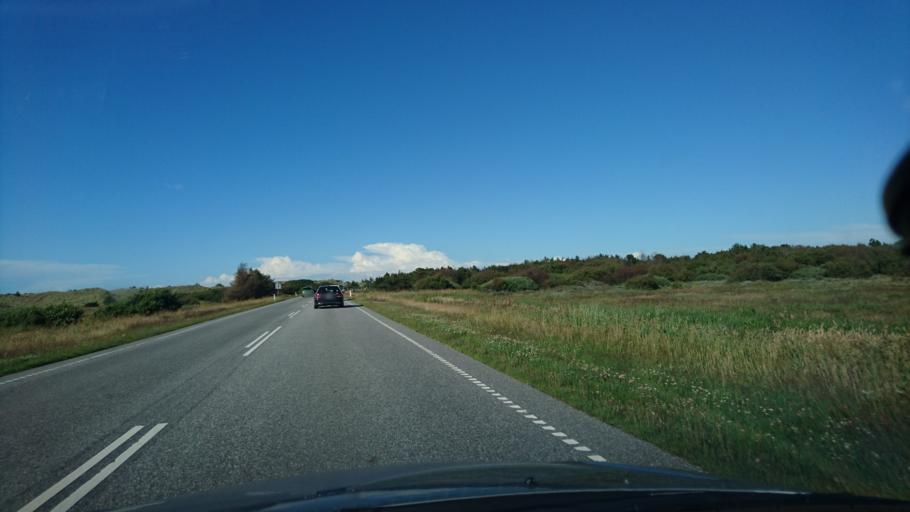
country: DK
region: North Denmark
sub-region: Frederikshavn Kommune
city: Skagen
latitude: 57.7229
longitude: 10.5412
